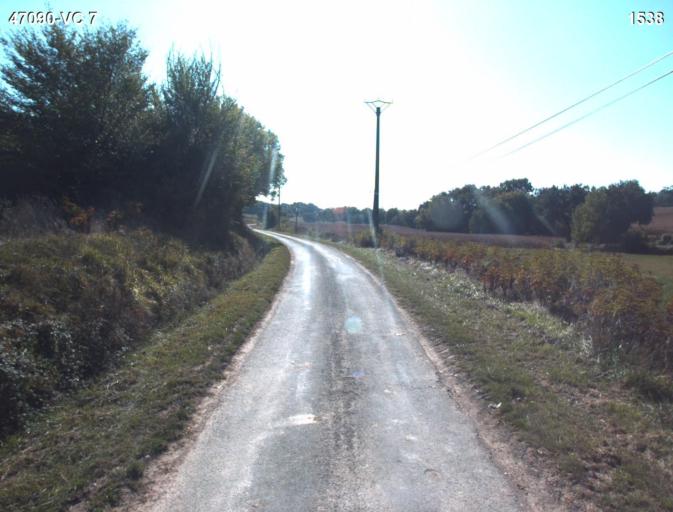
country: FR
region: Aquitaine
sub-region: Departement du Lot-et-Garonne
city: Vianne
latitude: 44.1821
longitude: 0.3588
